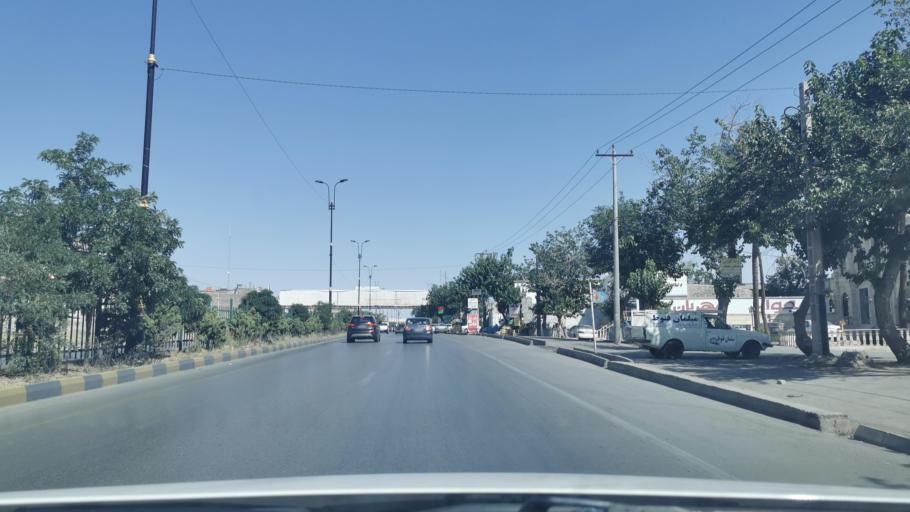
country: IR
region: Razavi Khorasan
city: Torqabeh
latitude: 36.3973
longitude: 59.3948
